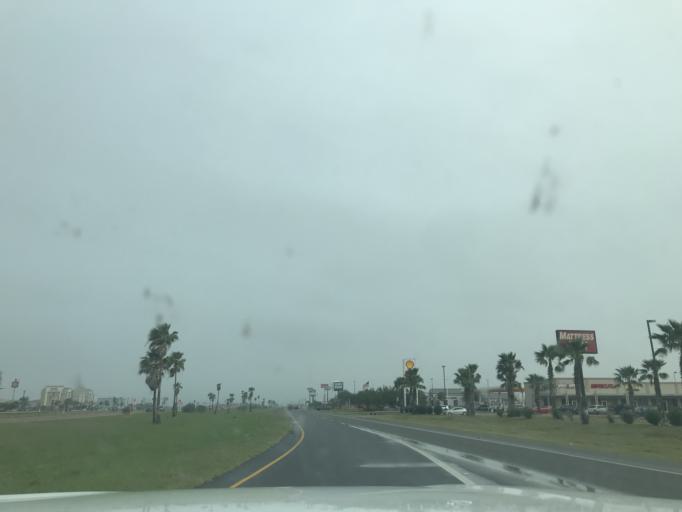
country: US
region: Texas
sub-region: San Patricio County
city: Portland
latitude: 27.8897
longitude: -97.3120
